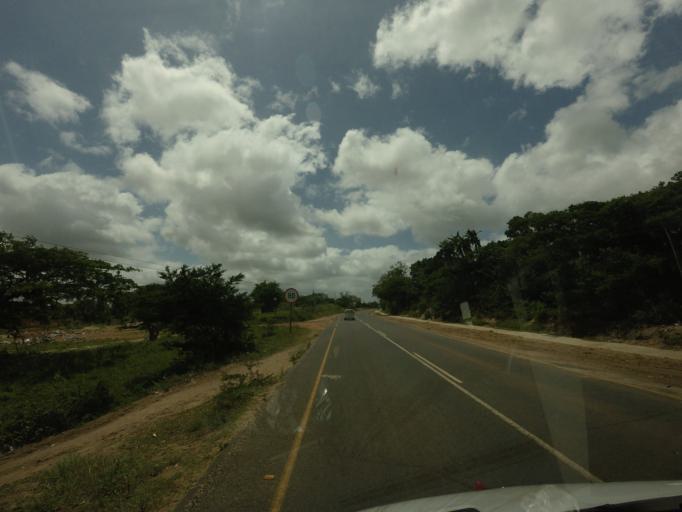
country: ZA
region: KwaZulu-Natal
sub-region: uMkhanyakude District Municipality
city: Mtubatuba
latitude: -28.3768
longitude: 32.3728
